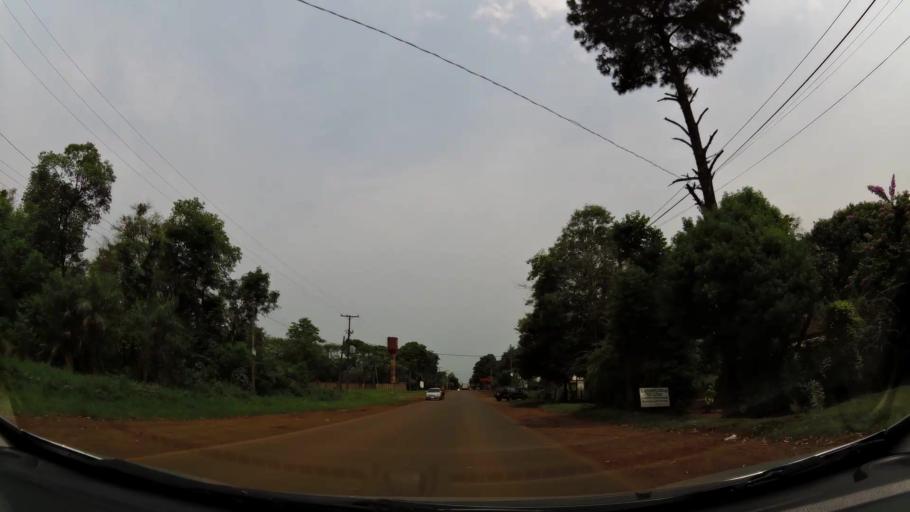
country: AR
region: Misiones
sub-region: Departamento de Iguazu
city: Puerto Iguazu
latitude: -25.5854
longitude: -54.6027
